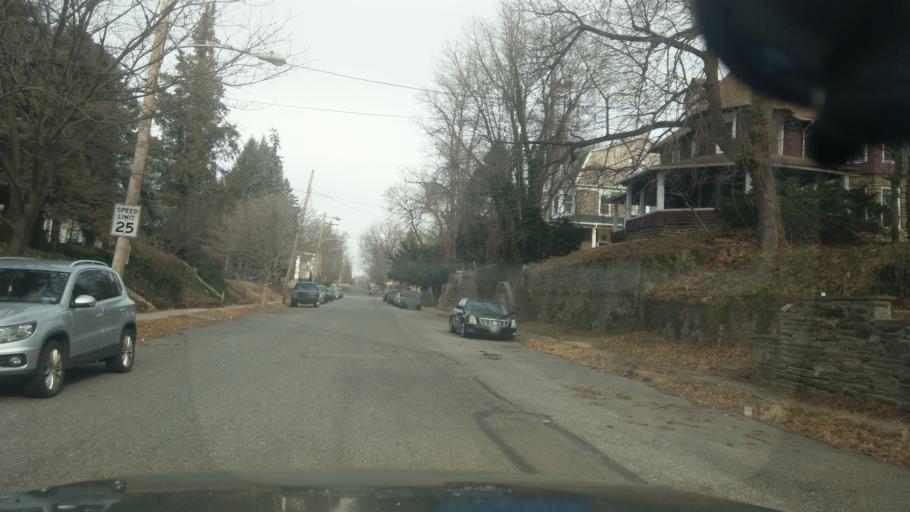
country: US
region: Pennsylvania
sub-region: Montgomery County
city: Jenkintown
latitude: 40.0510
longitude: -75.1322
